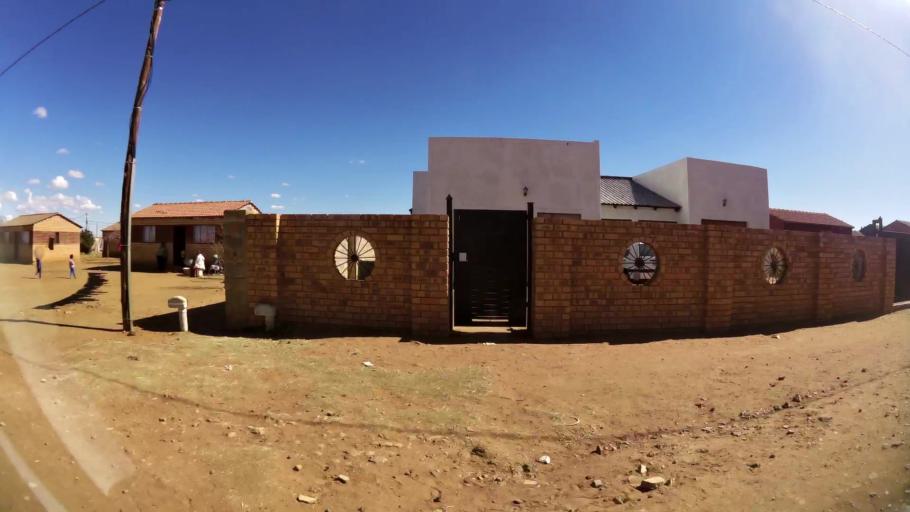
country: ZA
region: North-West
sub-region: Dr Kenneth Kaunda District Municipality
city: Klerksdorp
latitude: -26.8674
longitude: 26.5681
